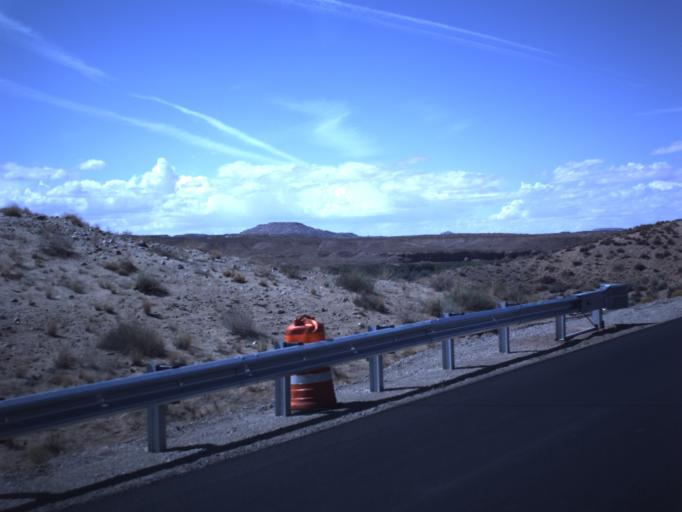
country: US
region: Utah
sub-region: San Juan County
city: Blanding
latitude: 37.2379
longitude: -109.2305
